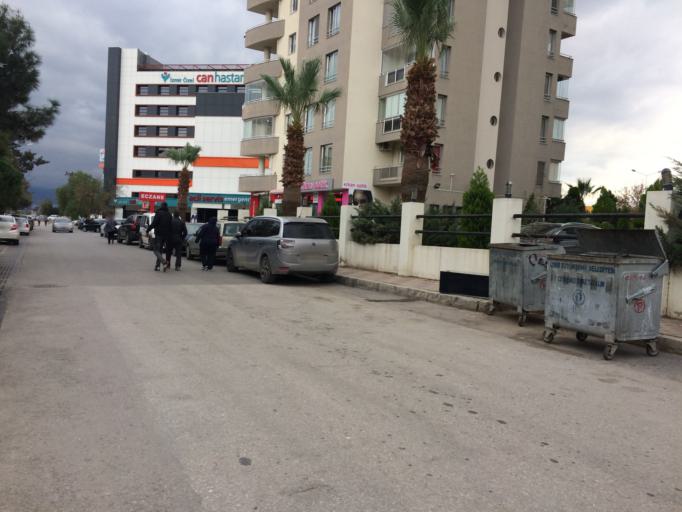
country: TR
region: Izmir
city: Karsiyaka
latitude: 38.4839
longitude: 27.0590
